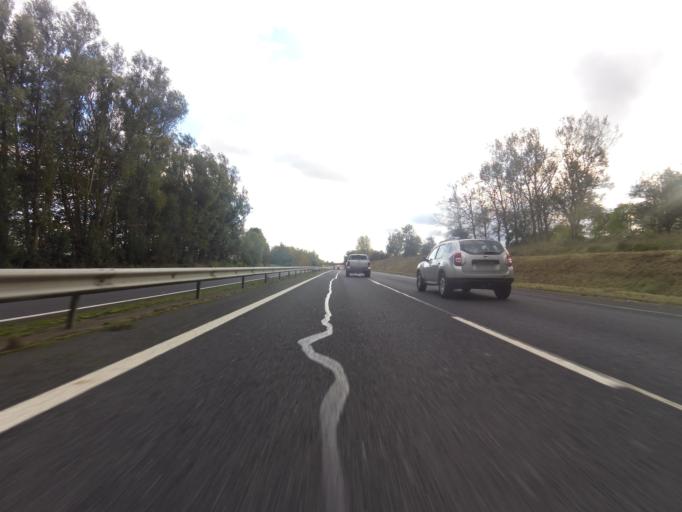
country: FR
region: Haute-Normandie
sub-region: Departement de la Seine-Maritime
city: Saint-Martin-Osmonville
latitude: 49.5762
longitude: 1.2753
